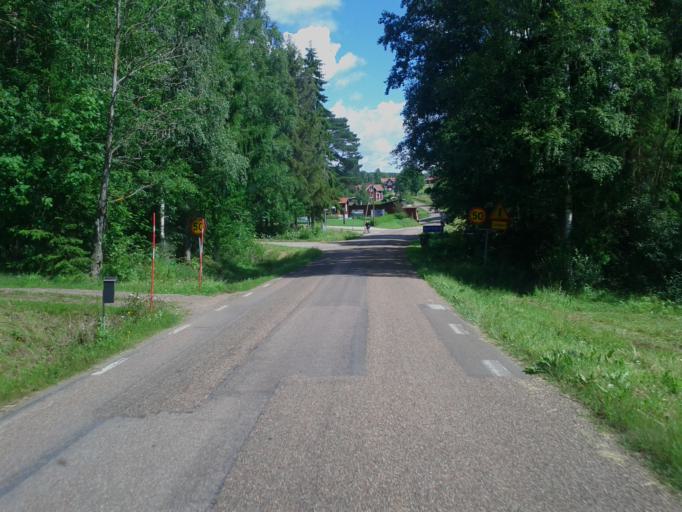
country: SE
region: Dalarna
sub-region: Rattviks Kommun
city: Vikarbyn
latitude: 60.9146
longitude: 15.0540
